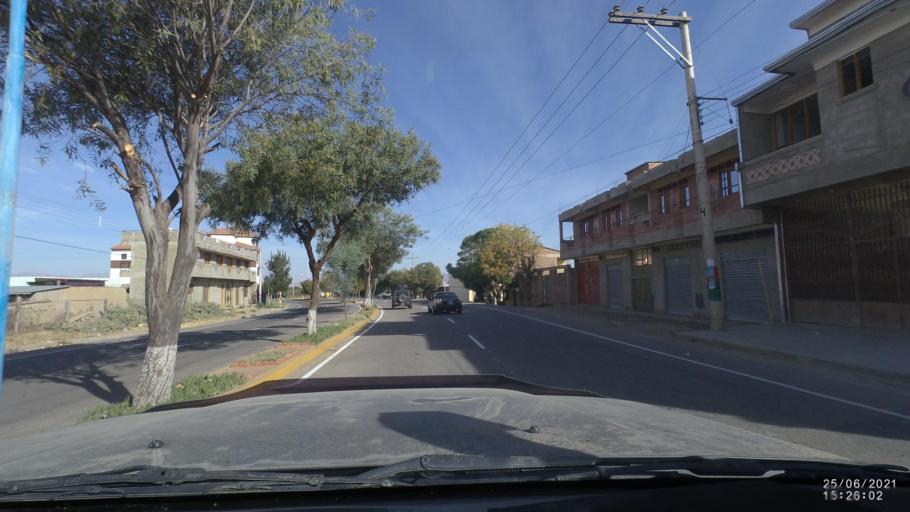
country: BO
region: Cochabamba
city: Cliza
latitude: -17.5349
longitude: -65.9619
